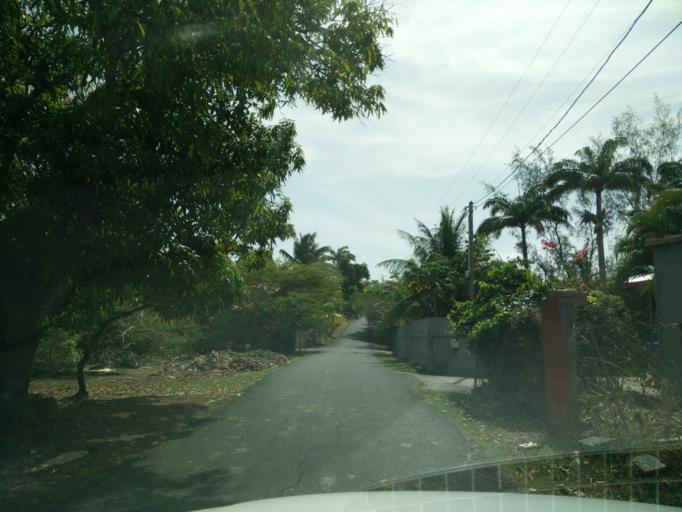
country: GP
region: Guadeloupe
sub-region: Guadeloupe
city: Sainte-Anne
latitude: 16.2434
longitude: -61.3373
